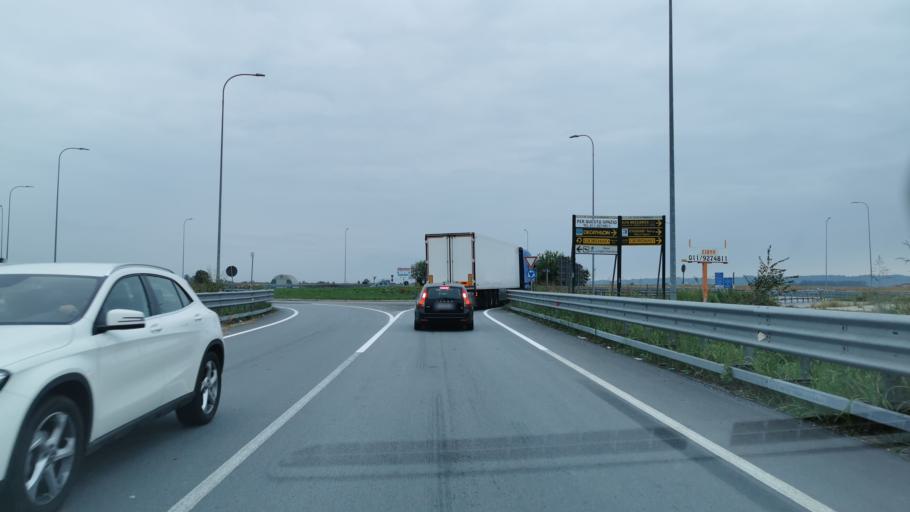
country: IT
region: Piedmont
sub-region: Provincia di Cuneo
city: Roreto
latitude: 44.6655
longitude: 7.8023
